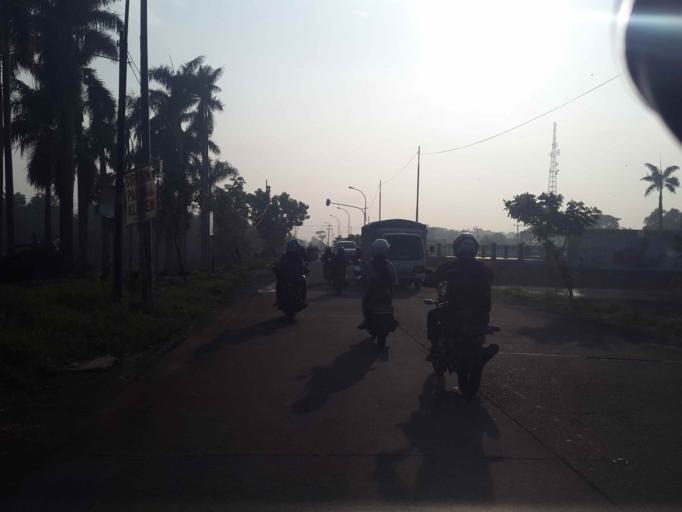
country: ID
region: West Java
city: Bekasi
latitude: -6.2774
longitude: 107.0653
